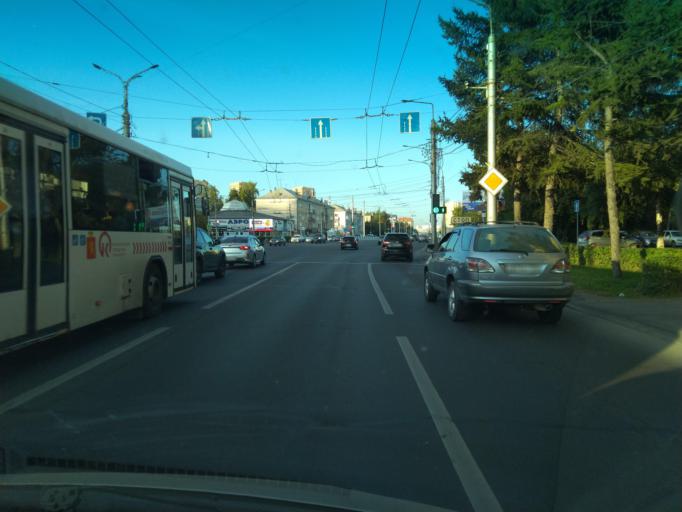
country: RU
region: Krasnoyarskiy
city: Krasnoyarsk
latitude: 56.0259
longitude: 92.9069
